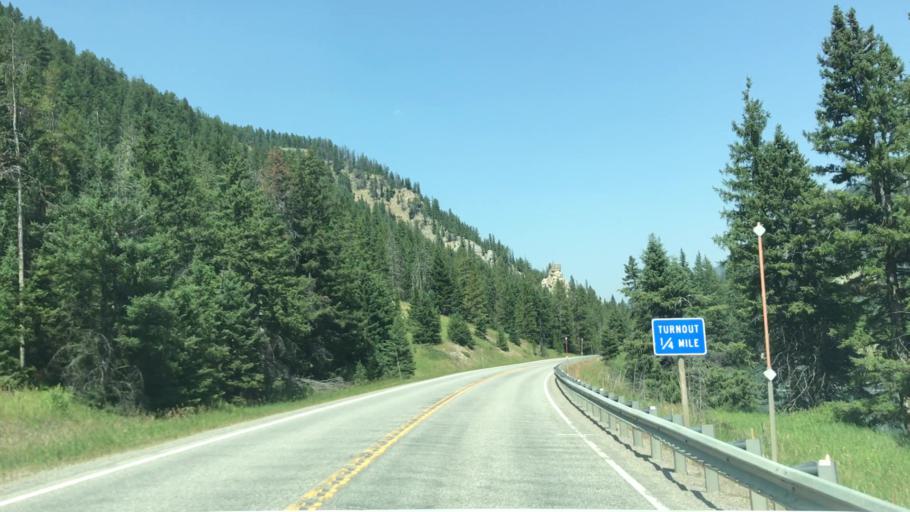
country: US
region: Montana
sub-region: Gallatin County
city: Big Sky
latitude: 45.0791
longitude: -111.2077
